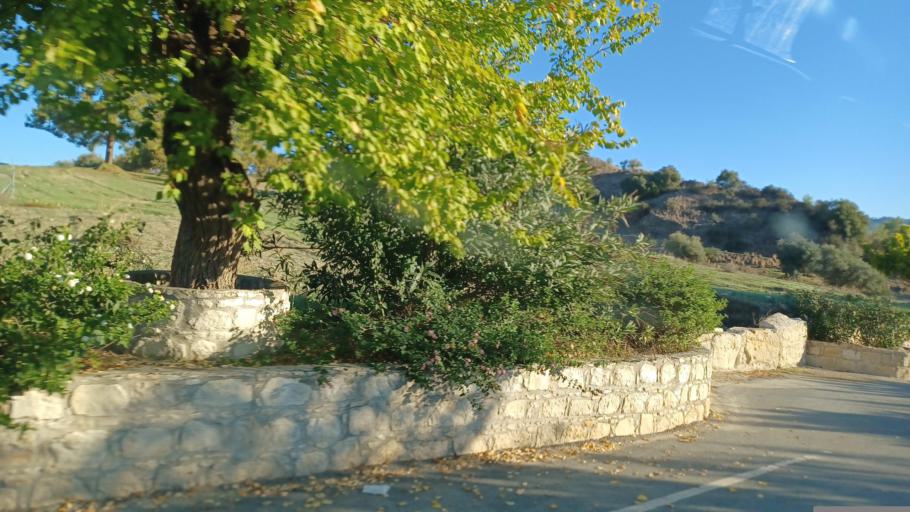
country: CY
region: Pafos
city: Polis
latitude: 34.9439
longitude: 32.5677
